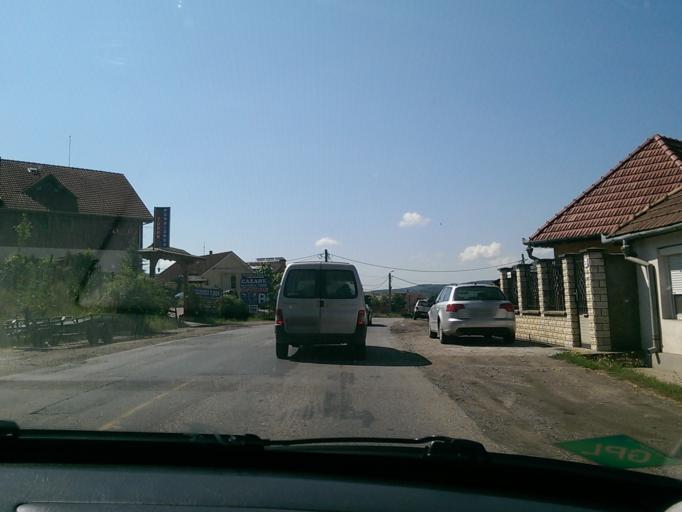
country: RO
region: Bihor
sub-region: Comuna Sanmartin
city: Sanmartin
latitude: 46.9876
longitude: 21.9853
